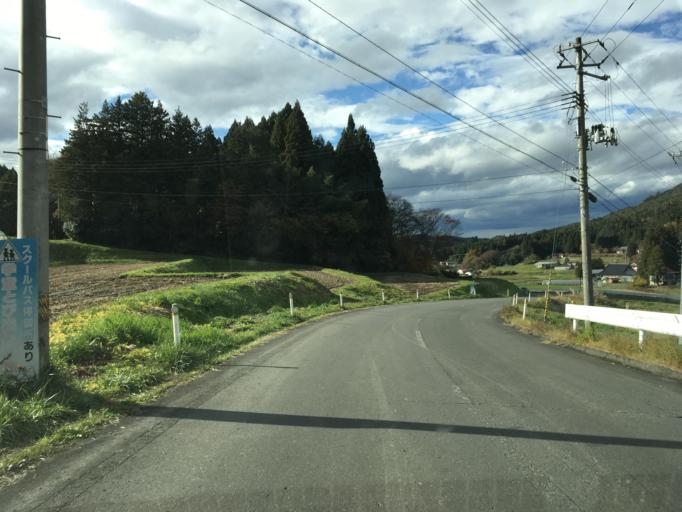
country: JP
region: Iwate
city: Ofunato
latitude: 38.8894
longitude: 141.4563
